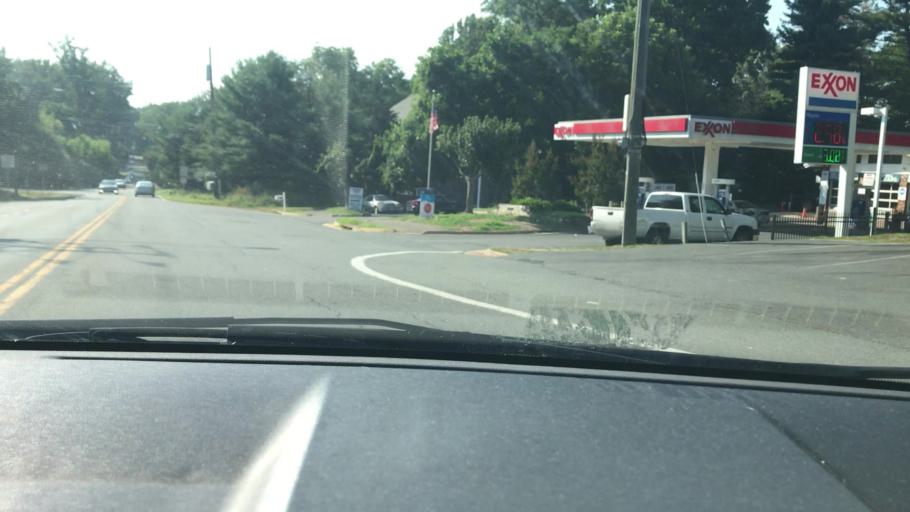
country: US
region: Virginia
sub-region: Fairfax County
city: Tysons Corner
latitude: 38.9529
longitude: -77.2263
